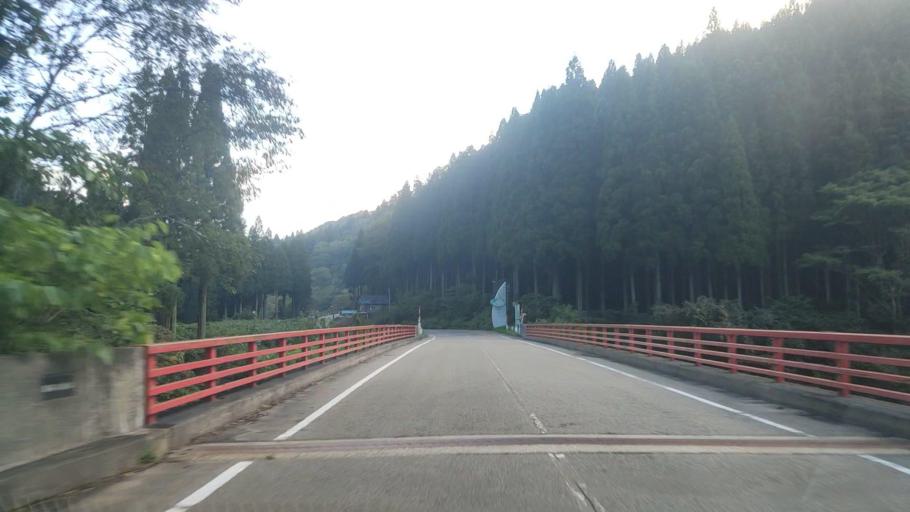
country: JP
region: Toyama
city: Yatsuomachi-higashikumisaka
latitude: 36.4958
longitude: 137.0495
